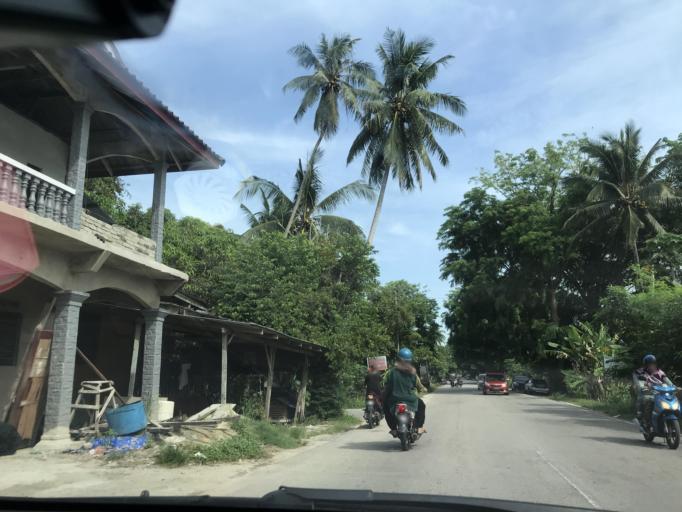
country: MY
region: Kelantan
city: Tumpat
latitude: 6.2124
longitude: 102.1308
